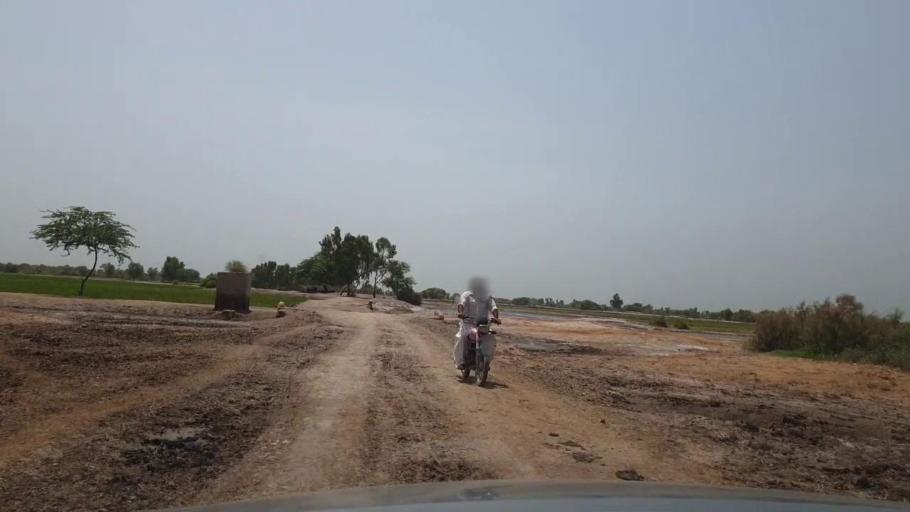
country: PK
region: Sindh
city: Madeji
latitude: 27.7729
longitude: 68.4056
